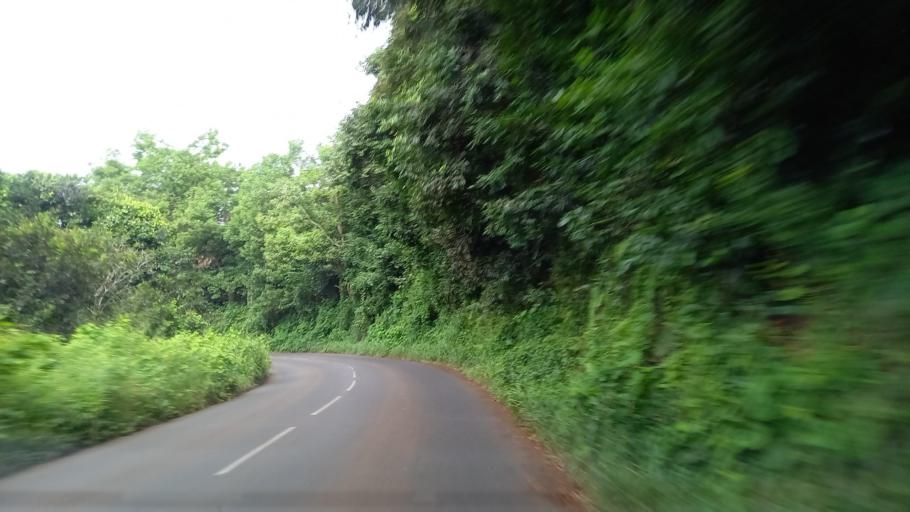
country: YT
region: Tsingoni
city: Tsingoni
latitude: -12.7859
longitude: 45.1536
